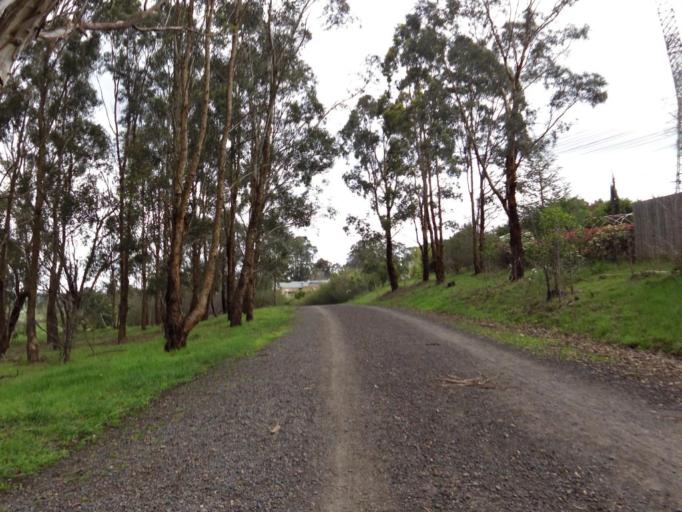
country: AU
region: Victoria
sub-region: Nillumbik
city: Eltham
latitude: -37.7450
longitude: 145.1640
